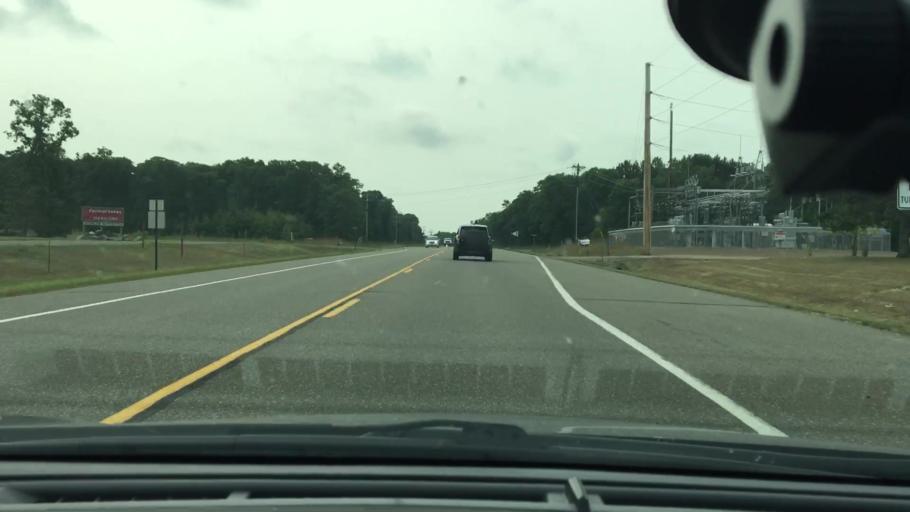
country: US
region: Minnesota
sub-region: Crow Wing County
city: Cross Lake
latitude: 46.6149
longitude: -94.1319
